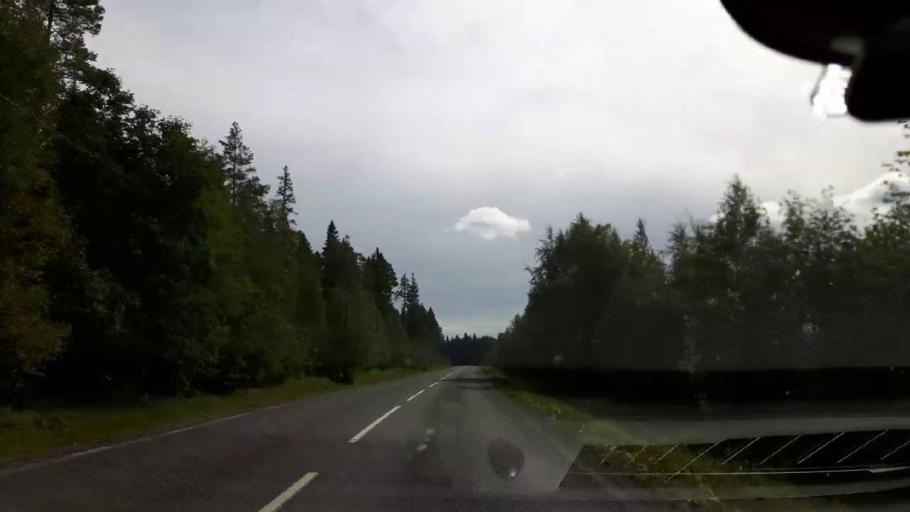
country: SE
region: Jaemtland
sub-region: Ragunda Kommun
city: Hammarstrand
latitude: 63.1430
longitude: 15.8588
